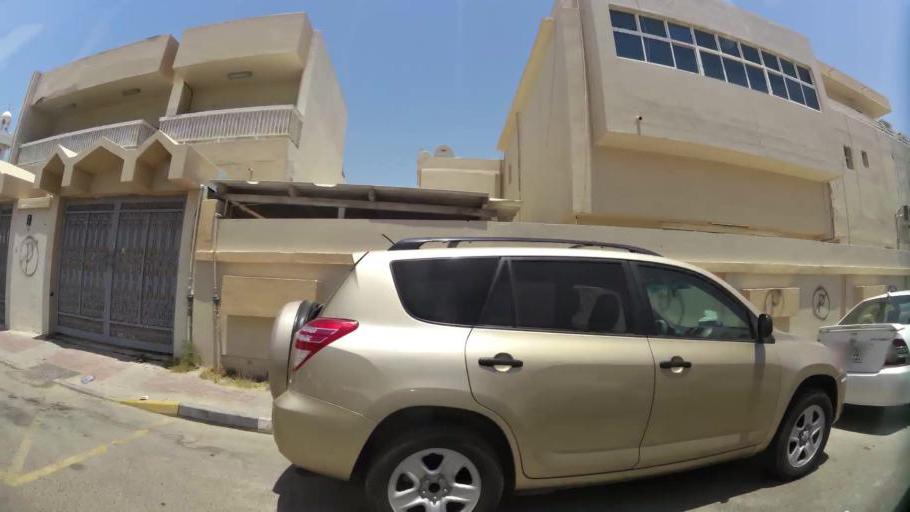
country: AE
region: Ash Shariqah
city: Sharjah
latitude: 25.2881
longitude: 55.3286
